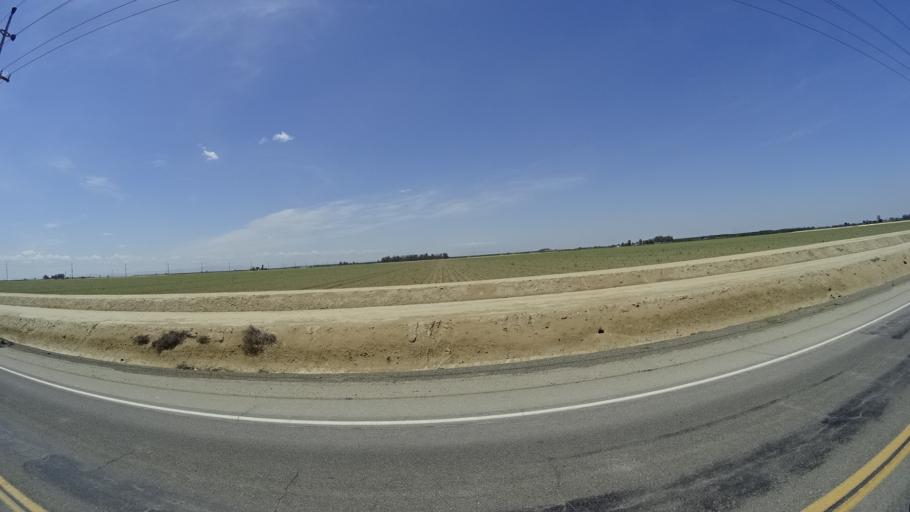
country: US
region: California
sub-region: Kings County
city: Home Garden
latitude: 36.2580
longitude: -119.6549
